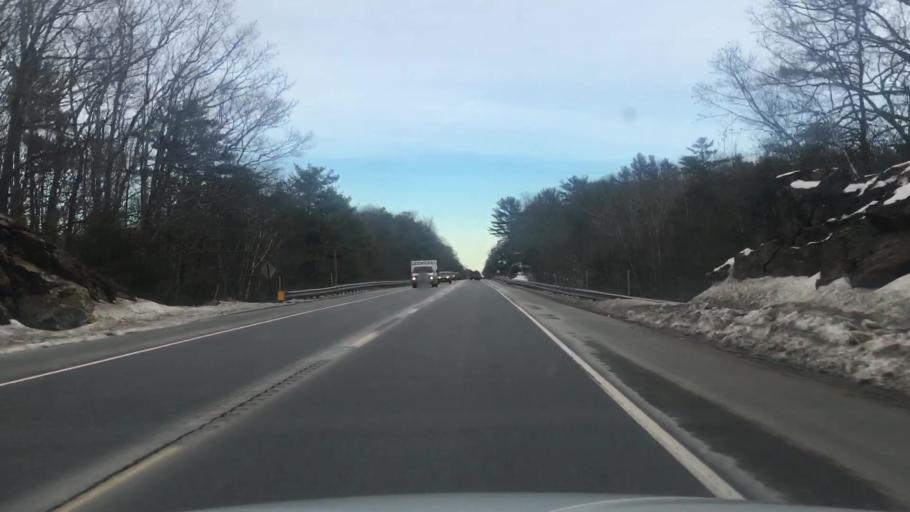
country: US
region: Maine
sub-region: Sagadahoc County
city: Woolwich
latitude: 43.9352
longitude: -69.7814
